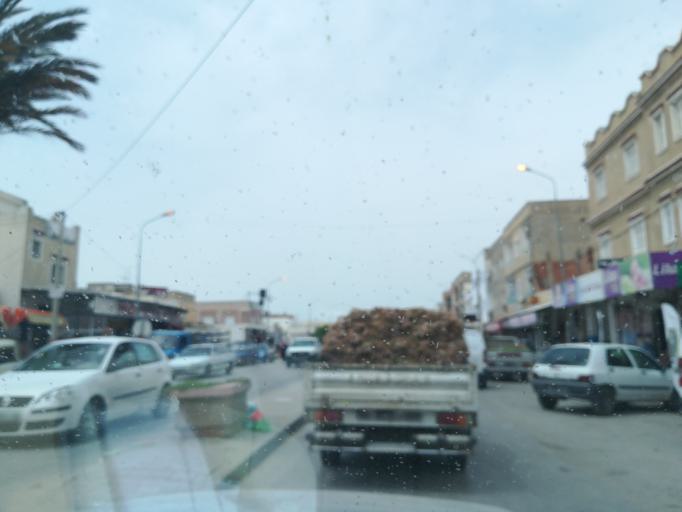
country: TN
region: Al Qayrawan
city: Kairouan
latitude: 35.6705
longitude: 10.0842
